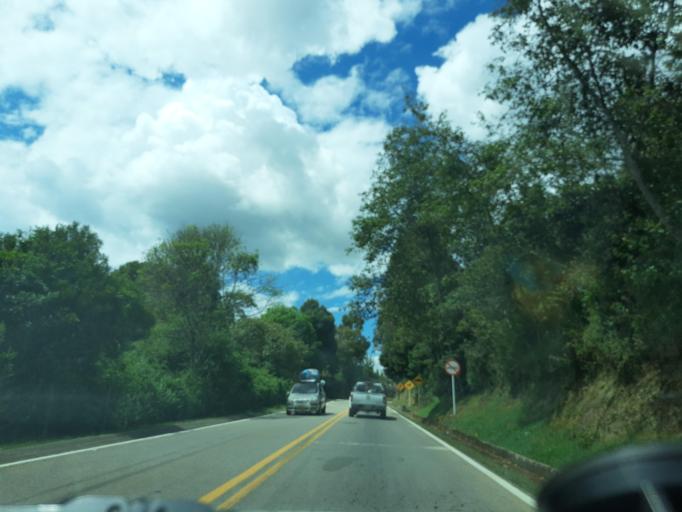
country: CO
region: Boyaca
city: Raquira
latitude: 5.5746
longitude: -73.6837
